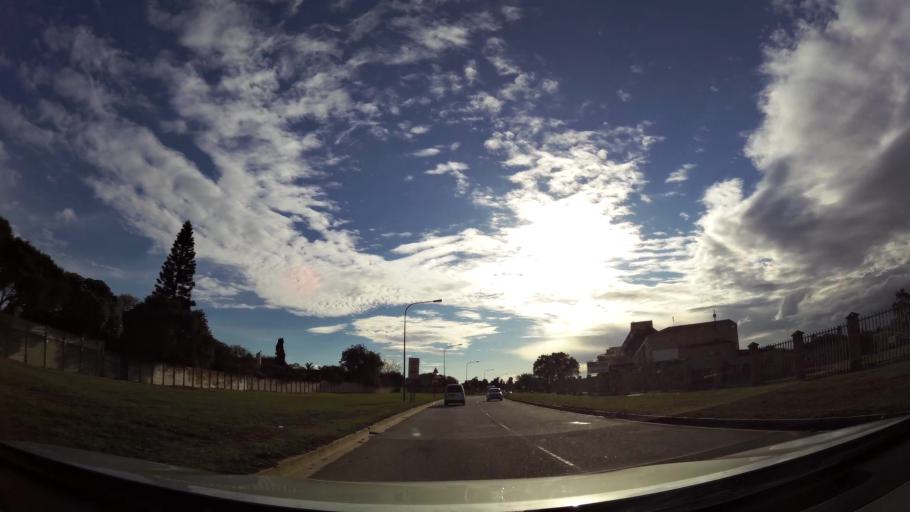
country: ZA
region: Eastern Cape
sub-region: Nelson Mandela Bay Metropolitan Municipality
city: Port Elizabeth
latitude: -33.9597
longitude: 25.4803
